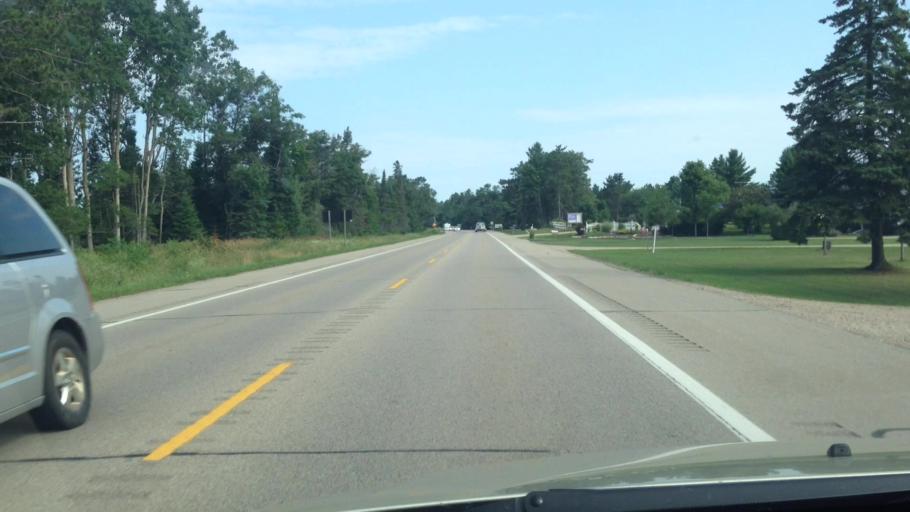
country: US
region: Michigan
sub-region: Delta County
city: Gladstone
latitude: 45.9156
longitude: -86.9325
